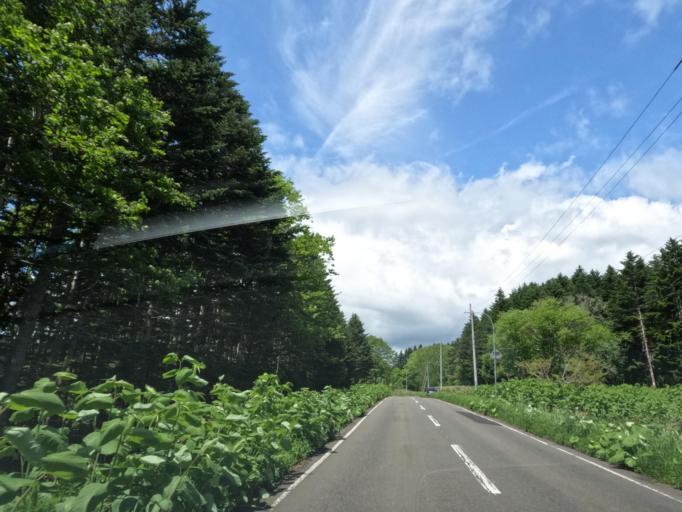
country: JP
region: Hokkaido
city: Tobetsu
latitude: 43.4130
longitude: 141.5875
